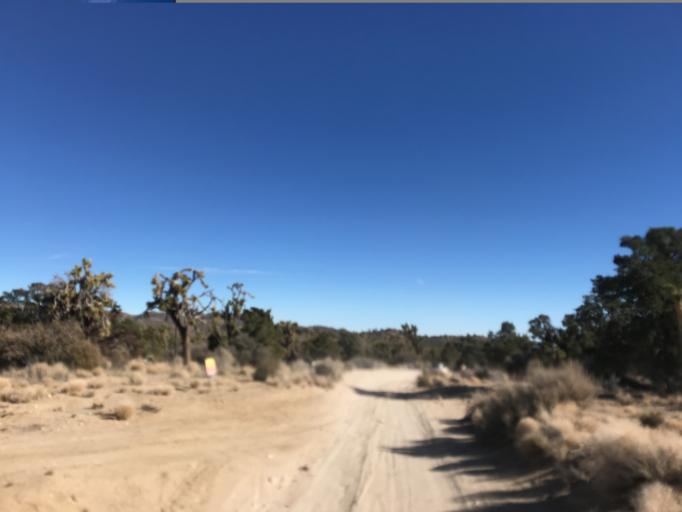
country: US
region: California
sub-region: San Bernardino County
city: Morongo Valley
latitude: 34.2341
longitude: -116.6458
